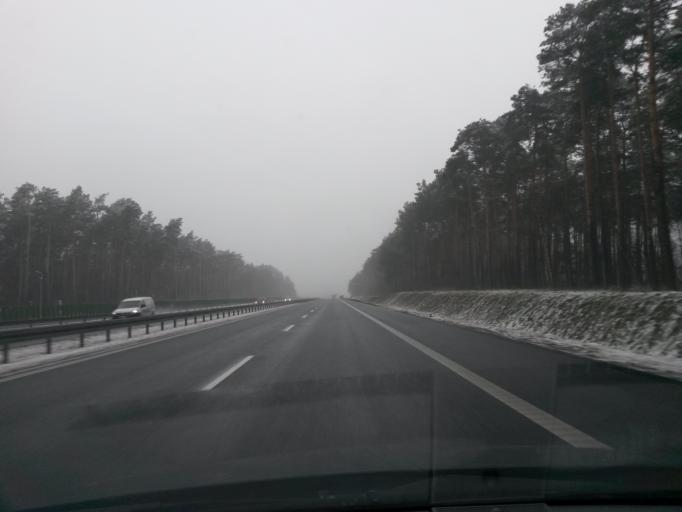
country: PL
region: Kujawsko-Pomorskie
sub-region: Powiat bydgoski
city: Biale Blota
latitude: 53.0795
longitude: 17.9113
